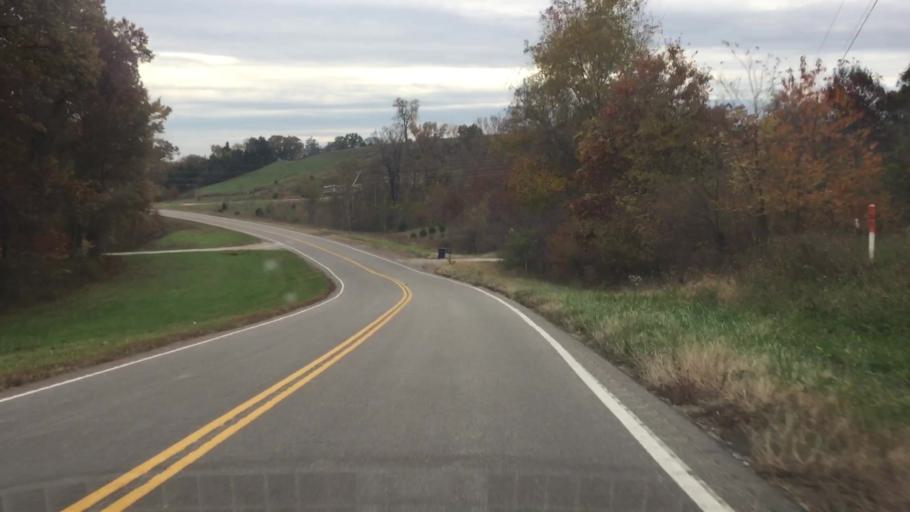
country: US
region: Missouri
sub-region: Callaway County
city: Fulton
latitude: 38.7118
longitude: -91.7397
